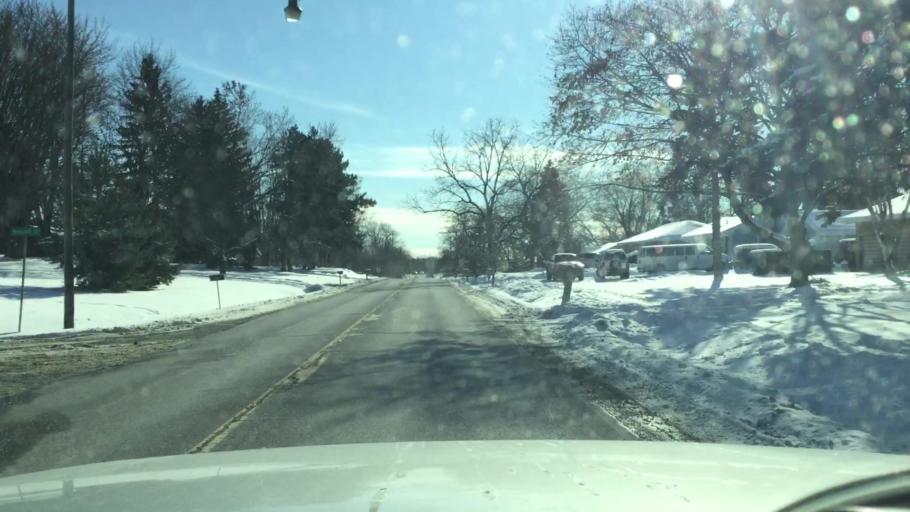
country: US
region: Michigan
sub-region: Oakland County
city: Keego Harbor
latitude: 42.6288
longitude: -83.3550
